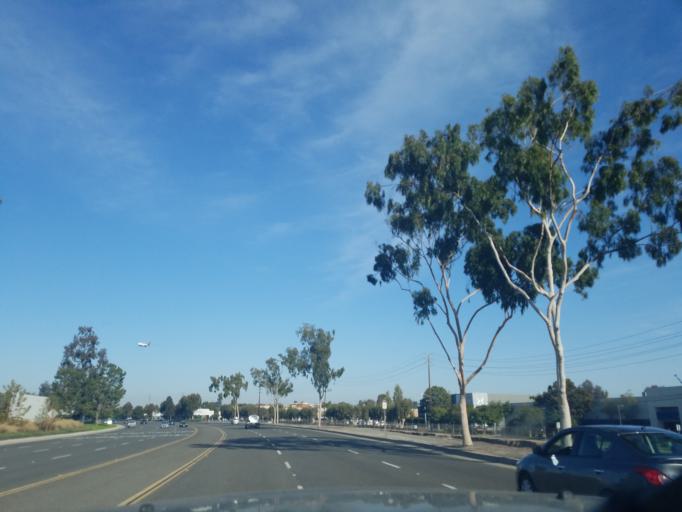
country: US
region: California
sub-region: Orange County
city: Irvine
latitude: 33.6896
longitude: -117.8533
